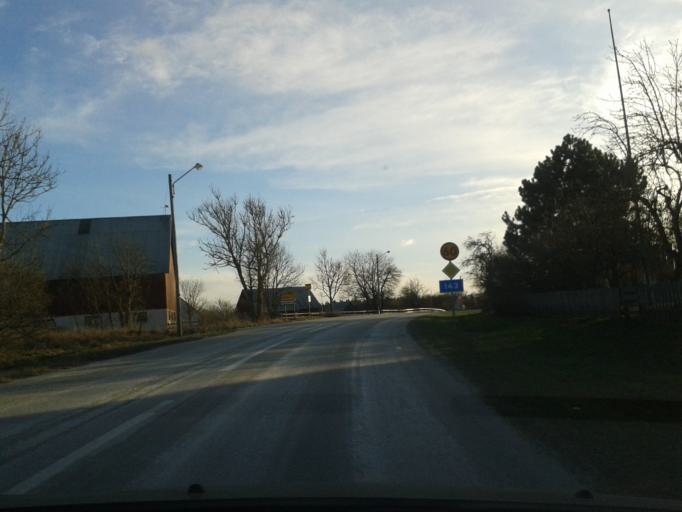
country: SE
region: Gotland
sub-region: Gotland
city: Hemse
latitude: 57.4289
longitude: 18.6306
